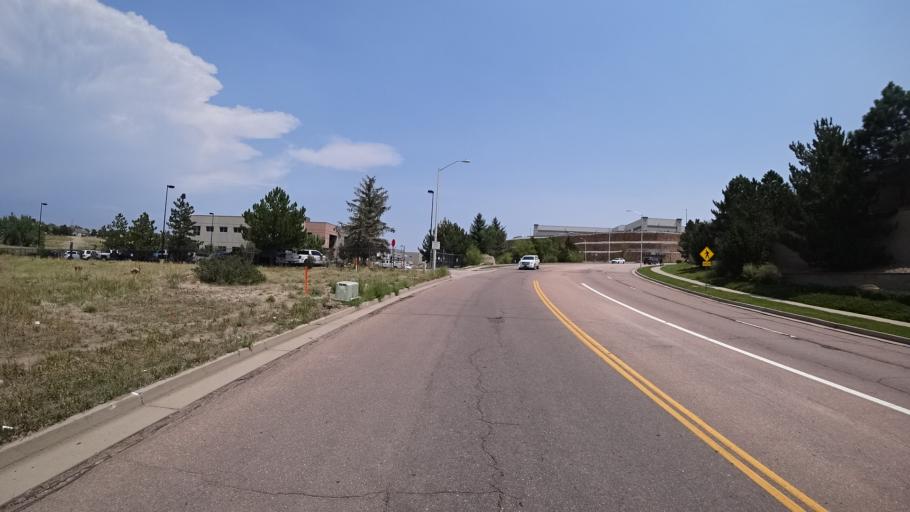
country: US
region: Colorado
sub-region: El Paso County
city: Black Forest
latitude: 38.9421
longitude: -104.7283
